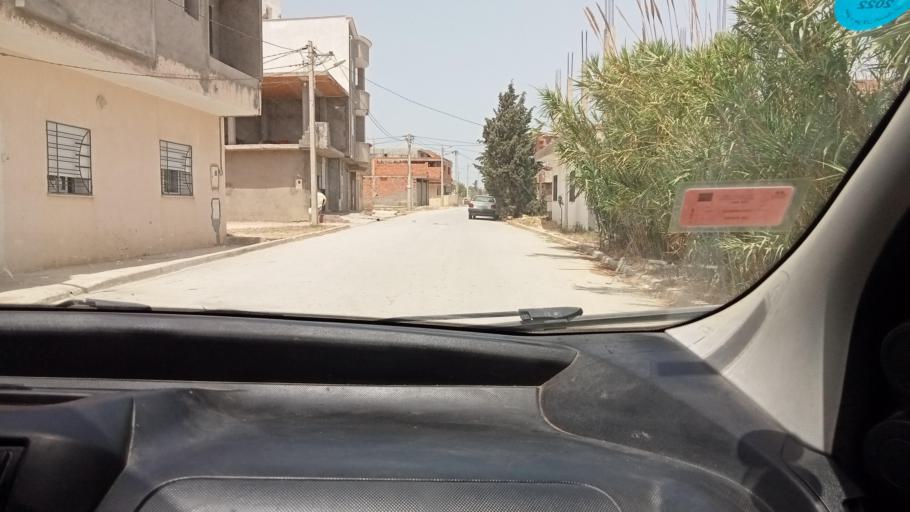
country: TN
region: Nabul
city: Qulaybiyah
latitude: 36.8626
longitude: 11.0854
